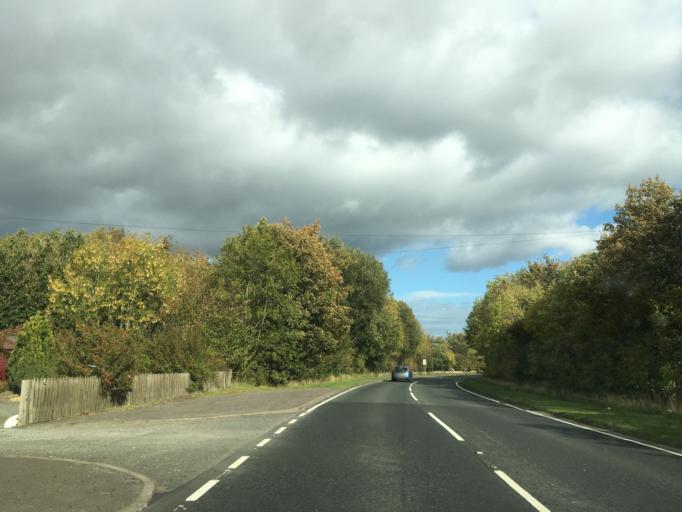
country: GB
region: Scotland
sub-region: Fife
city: Pathhead
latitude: 55.8943
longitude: -2.9671
